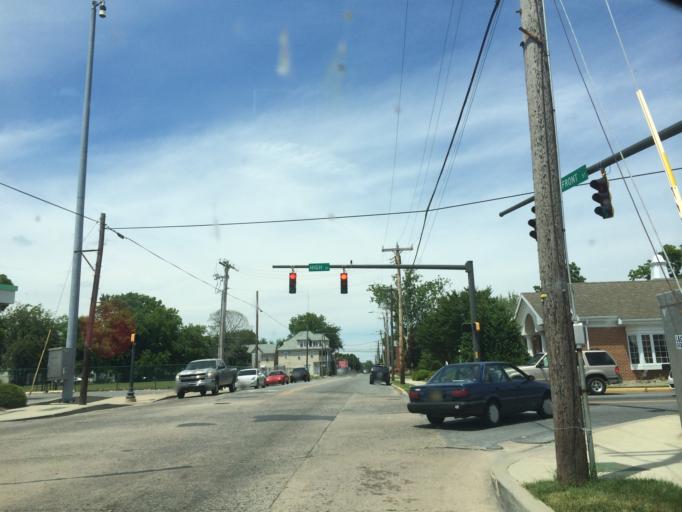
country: US
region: Delaware
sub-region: Sussex County
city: Seaford
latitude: 38.6421
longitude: -75.6090
